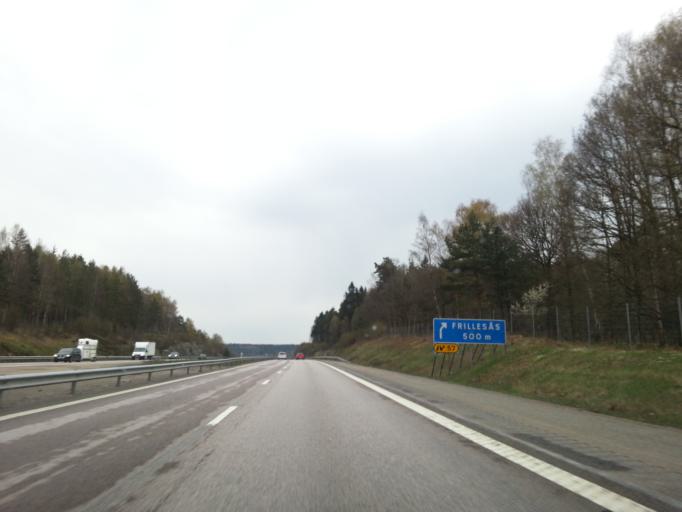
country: SE
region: Halland
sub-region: Kungsbacka Kommun
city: Frillesas
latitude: 57.3365
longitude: 12.2058
